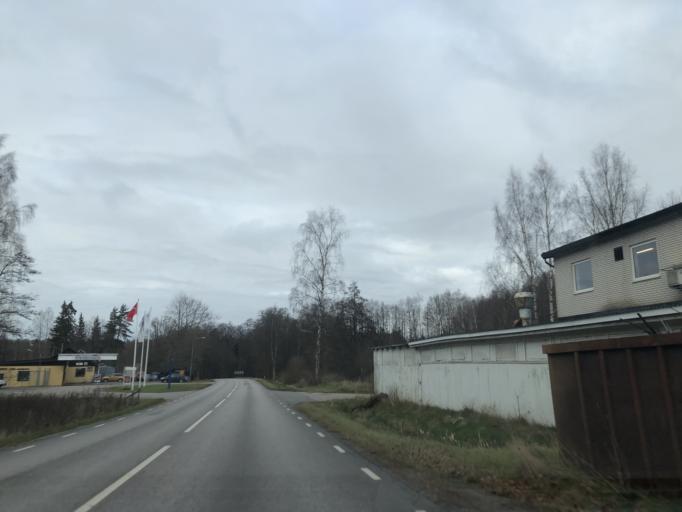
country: SE
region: Vaestra Goetaland
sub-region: Ulricehamns Kommun
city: Ulricehamn
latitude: 57.6772
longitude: 13.4001
